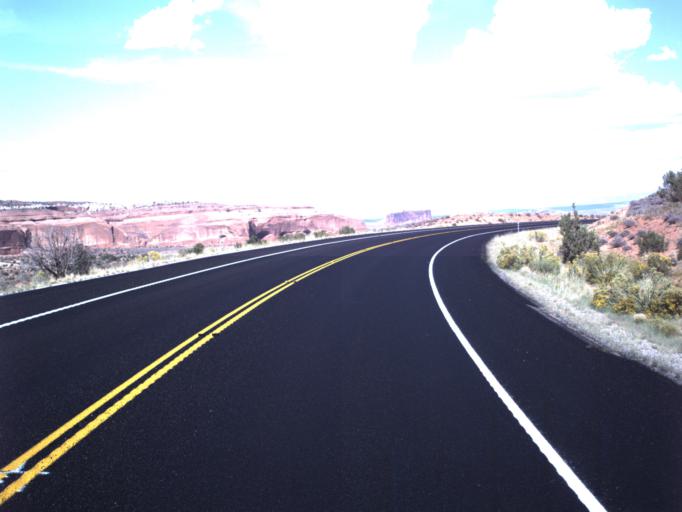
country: US
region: Utah
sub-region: Grand County
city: Moab
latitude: 38.6262
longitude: -109.8085
